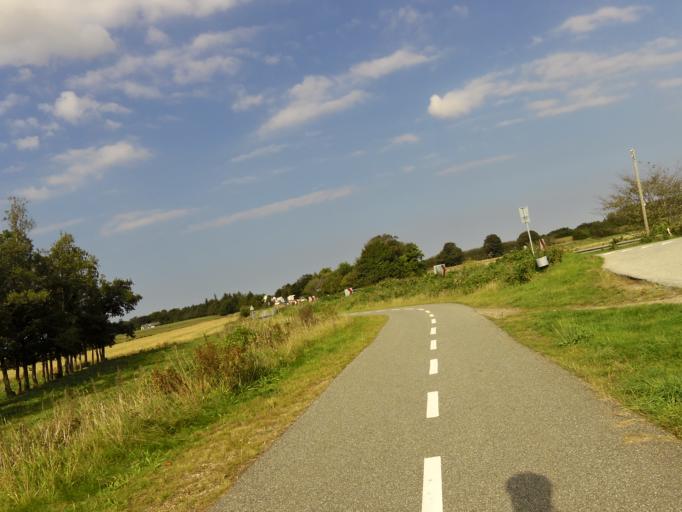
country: DK
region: South Denmark
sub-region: Vejen Kommune
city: Vejen
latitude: 55.4424
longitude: 9.1362
